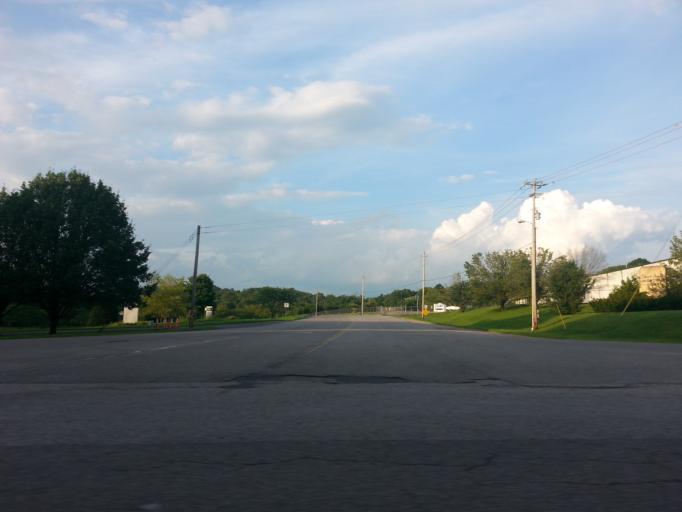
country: US
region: Tennessee
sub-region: Anderson County
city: Norris
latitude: 36.1807
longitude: -84.0525
